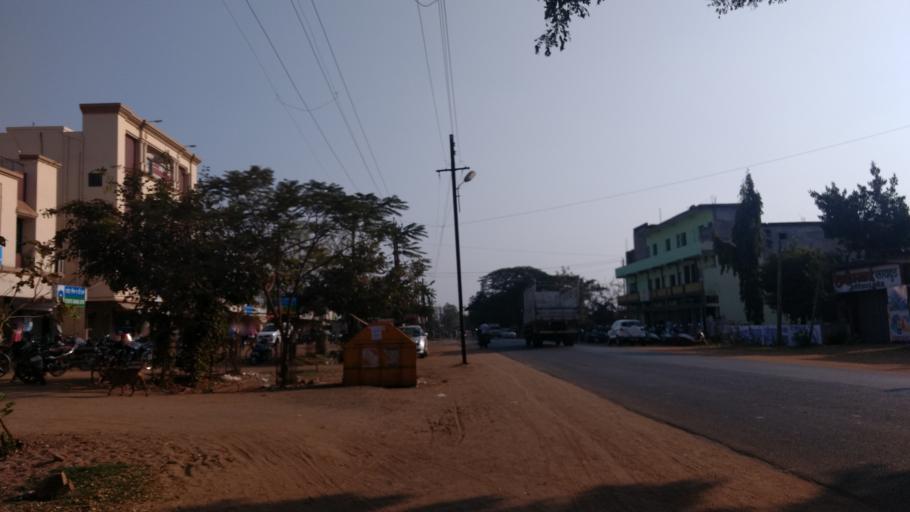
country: IN
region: Maharashtra
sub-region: Bhandara
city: Pauni
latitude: 20.6128
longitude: 79.8558
